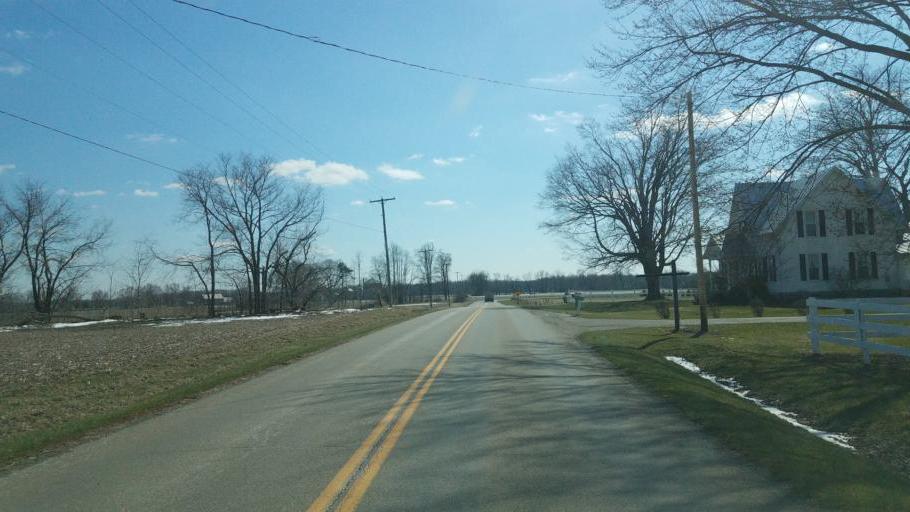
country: US
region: Ohio
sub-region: Knox County
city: Fredericktown
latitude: 40.4568
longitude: -82.5418
